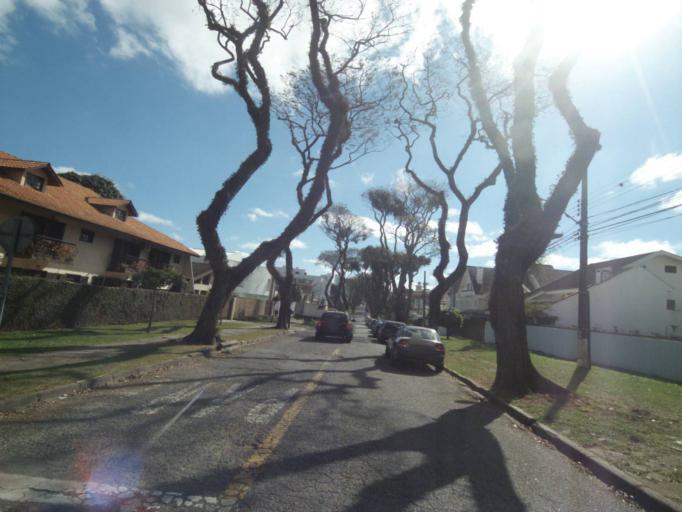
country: BR
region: Parana
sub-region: Curitiba
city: Curitiba
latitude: -25.4554
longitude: -49.2761
